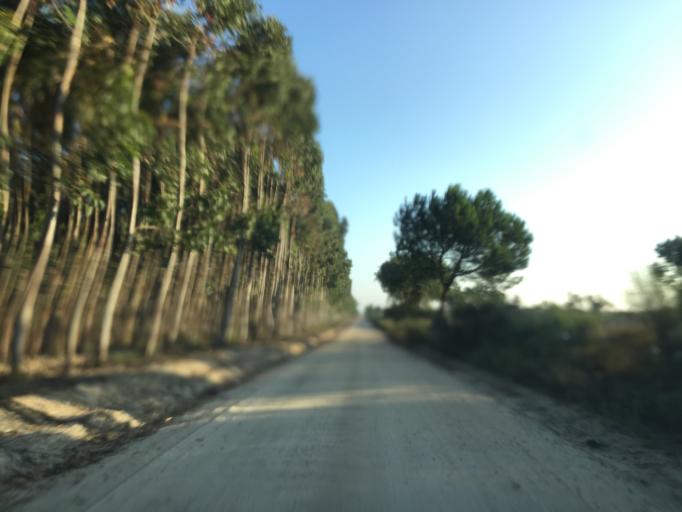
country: PT
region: Portalegre
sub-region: Ponte de Sor
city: Santo Andre
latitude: 39.1049
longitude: -8.3439
